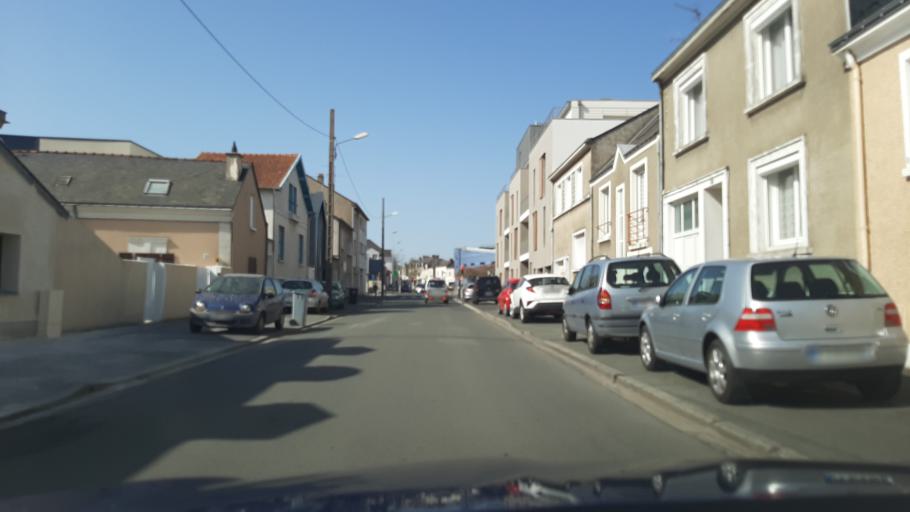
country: FR
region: Pays de la Loire
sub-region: Departement de Maine-et-Loire
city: Les Ponts-de-Ce
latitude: 47.4515
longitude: -0.5246
